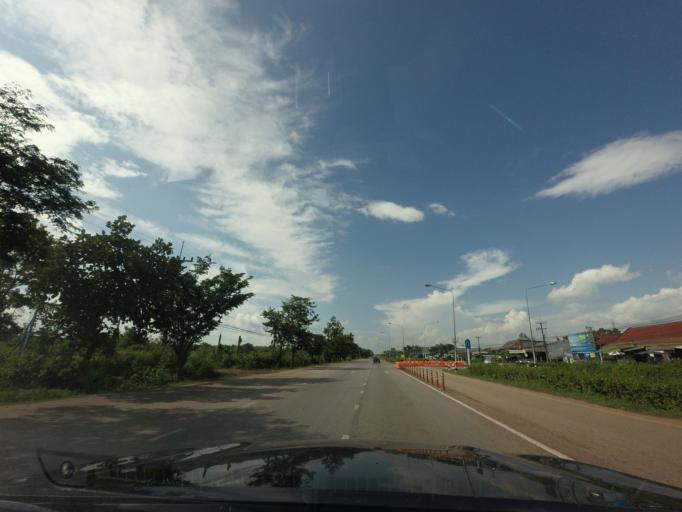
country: TH
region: Nong Khai
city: Sa Khrai
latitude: 17.6899
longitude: 102.7830
